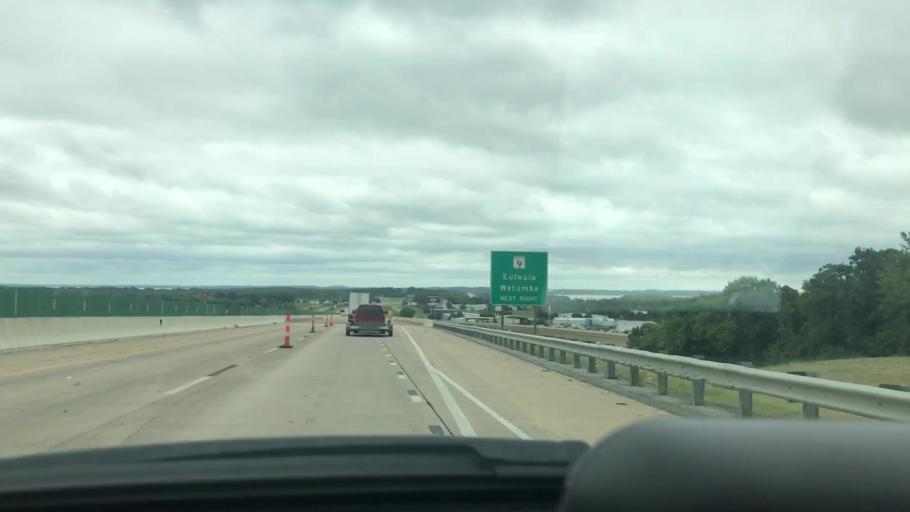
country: US
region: Oklahoma
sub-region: McIntosh County
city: Eufaula
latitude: 35.2915
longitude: -95.5931
